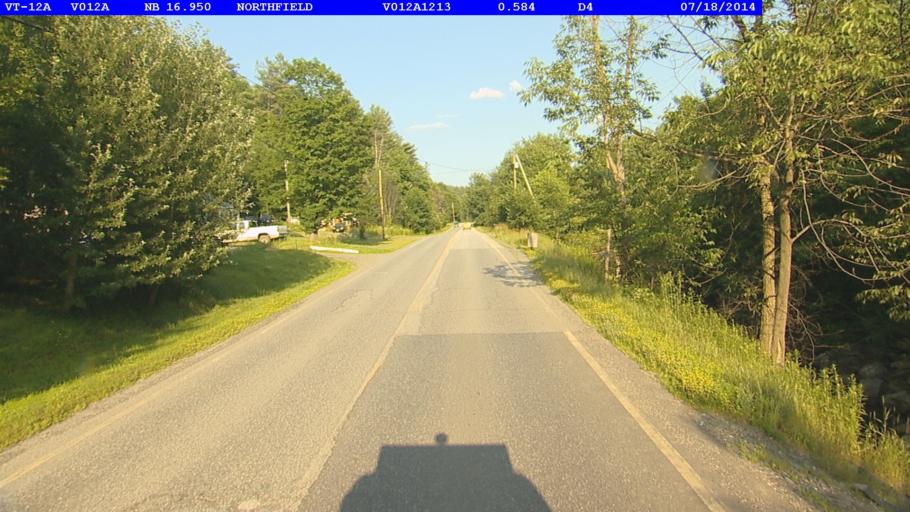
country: US
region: Vermont
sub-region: Washington County
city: Northfield
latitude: 44.1181
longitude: -72.7151
